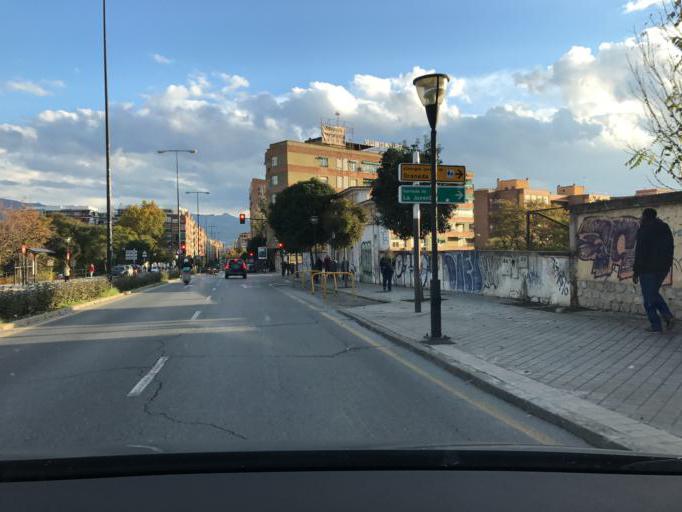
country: ES
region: Andalusia
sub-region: Provincia de Granada
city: Granada
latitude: 37.1847
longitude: -3.6147
